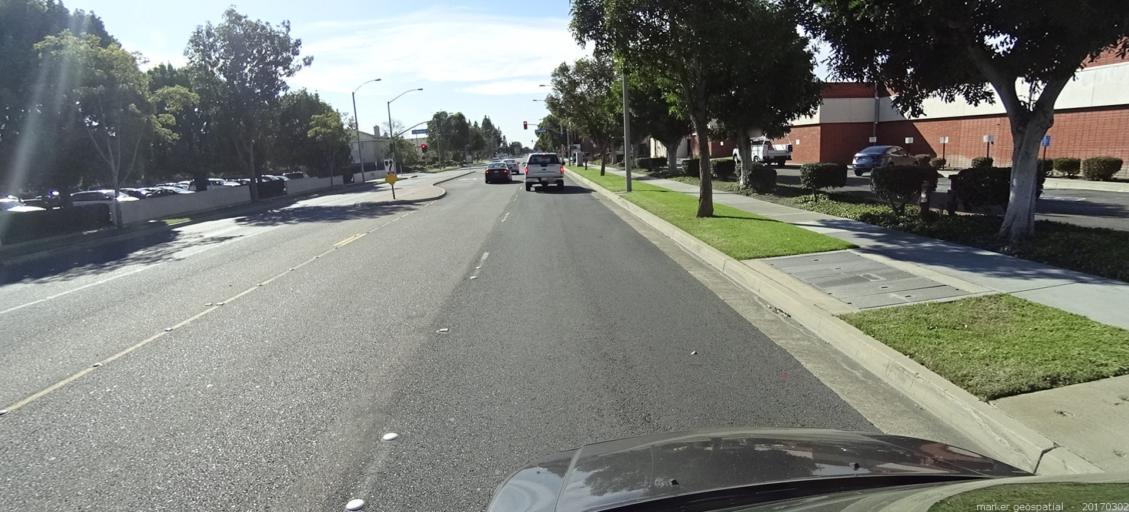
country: US
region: California
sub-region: Orange County
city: Stanton
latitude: 33.8248
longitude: -117.9945
